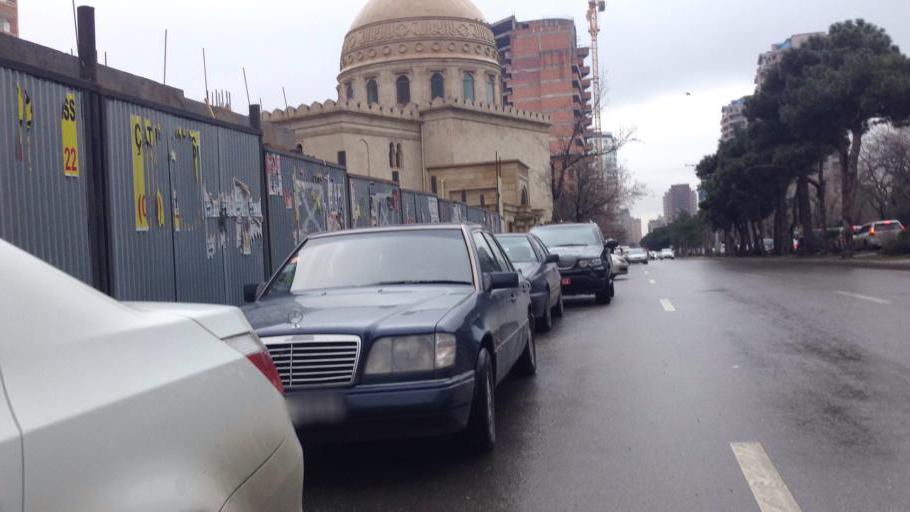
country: AZ
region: Baki
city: Baku
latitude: 40.3865
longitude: 49.8372
